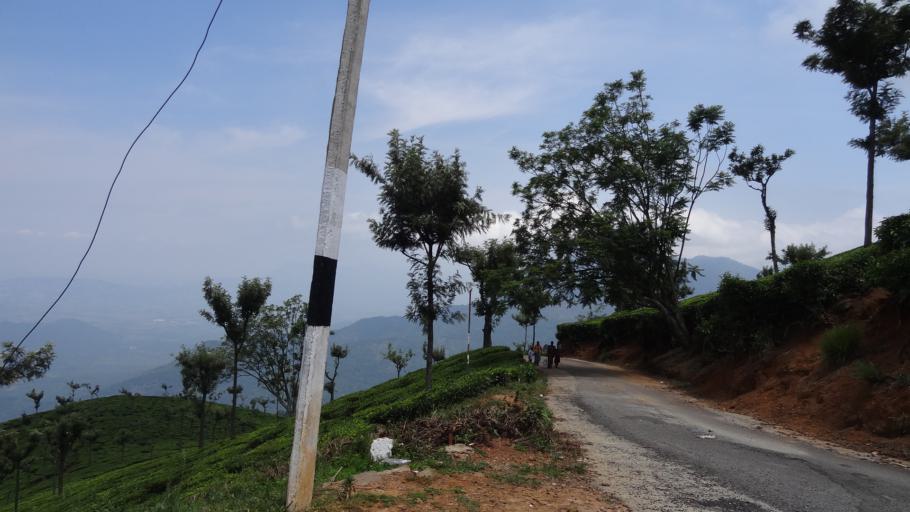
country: IN
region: Tamil Nadu
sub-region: Nilgiri
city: Kotagiri
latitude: 11.3658
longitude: 76.8560
